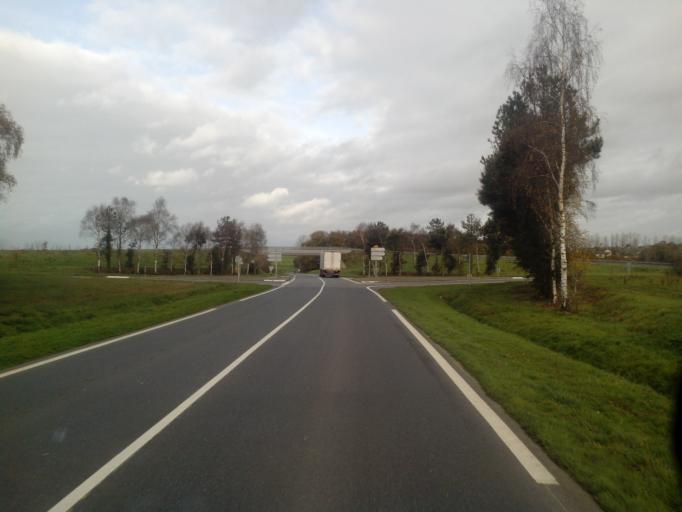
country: FR
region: Brittany
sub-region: Departement d'Ille-et-Vilaine
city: Gael
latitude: 48.1286
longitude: -2.2327
